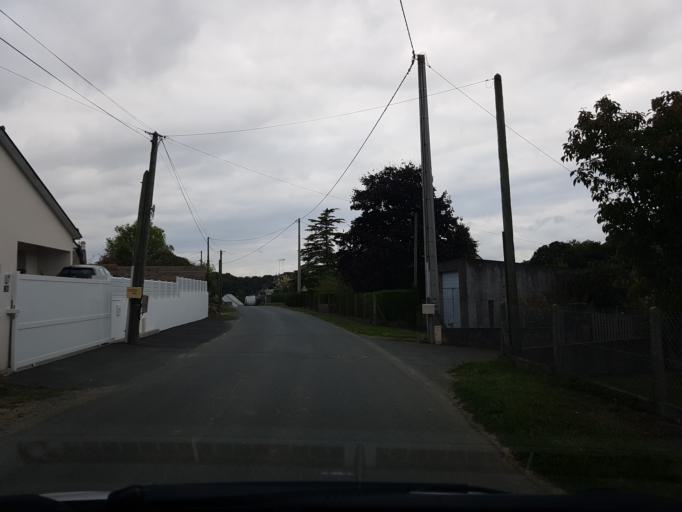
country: FR
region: Brittany
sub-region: Departement des Cotes-d'Armor
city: Pledran
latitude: 48.4644
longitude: -2.7491
